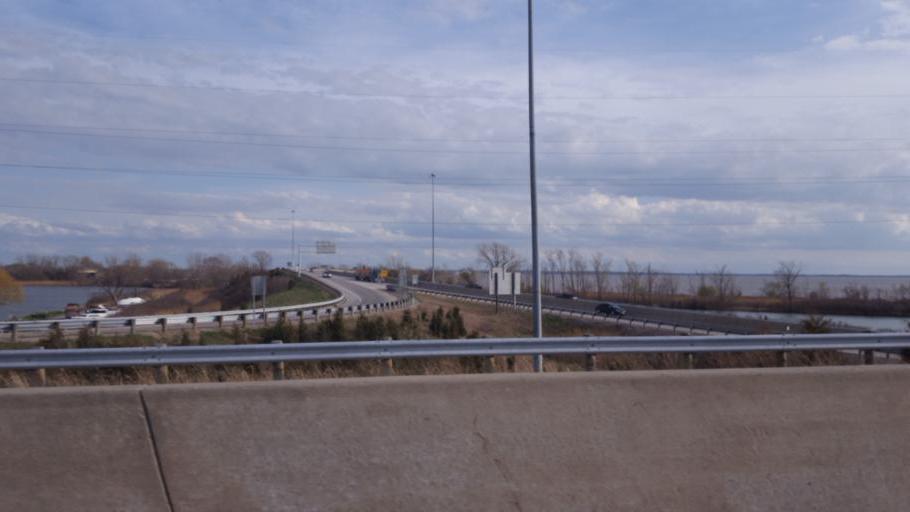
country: US
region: Ohio
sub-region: Ottawa County
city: Port Clinton
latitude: 41.5036
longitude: -82.8384
